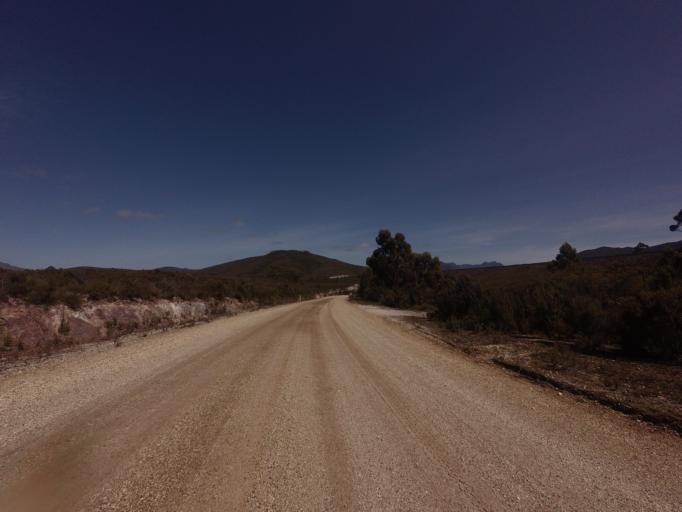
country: AU
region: Tasmania
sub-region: Huon Valley
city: Geeveston
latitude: -43.0324
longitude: 146.3020
